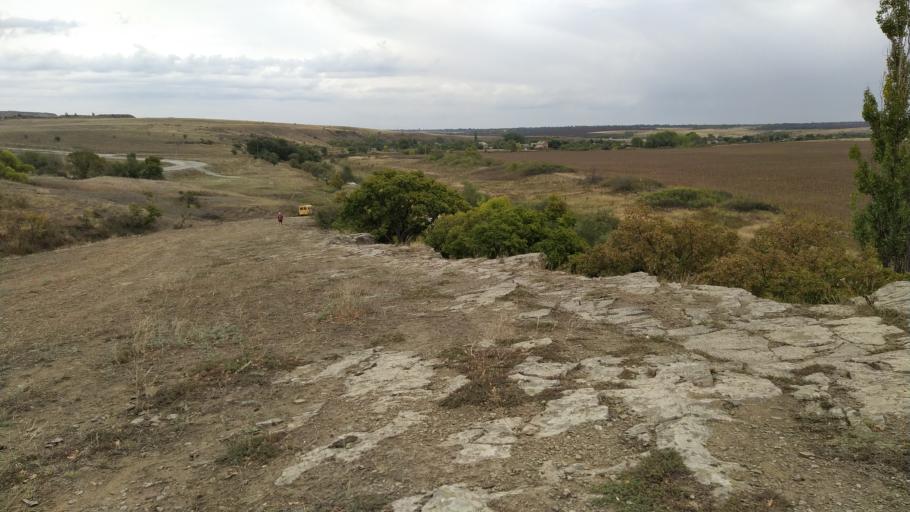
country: RU
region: Rostov
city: Gornyy
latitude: 47.8910
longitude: 40.2463
